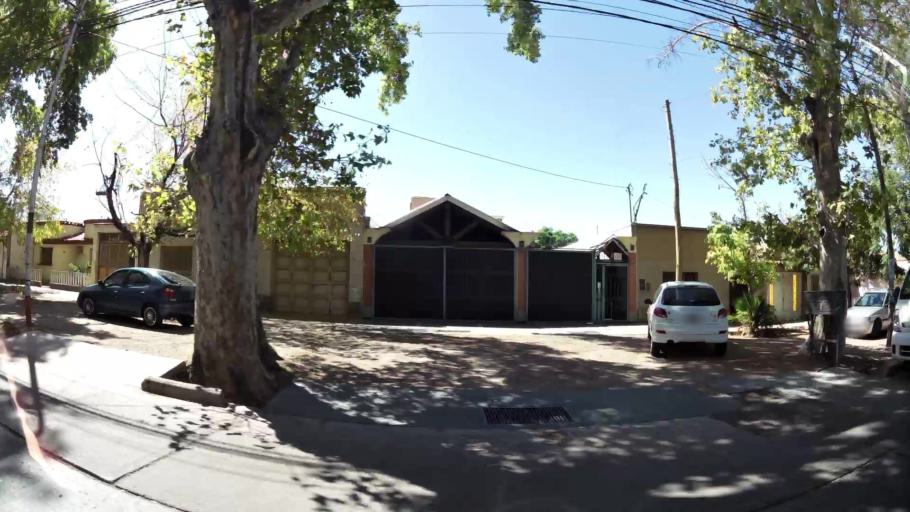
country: AR
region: Mendoza
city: Mendoza
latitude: -32.8957
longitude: -68.8123
